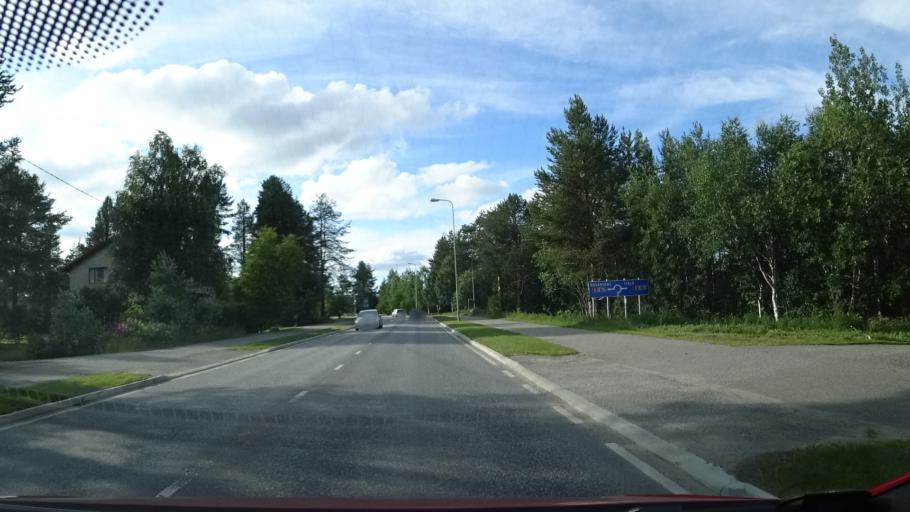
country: FI
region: Lapland
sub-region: Pohjois-Lappi
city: Sodankylae
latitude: 67.4202
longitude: 26.5904
